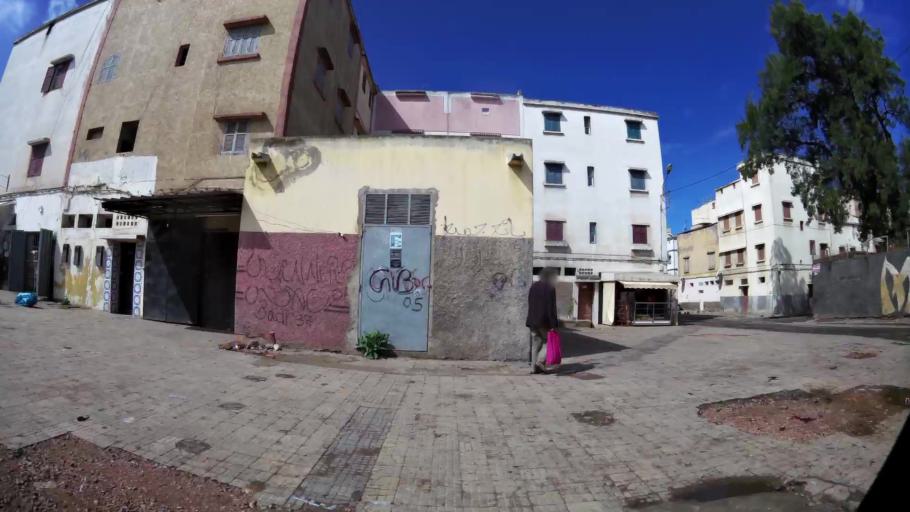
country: MA
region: Grand Casablanca
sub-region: Casablanca
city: Casablanca
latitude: 33.5702
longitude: -7.6762
